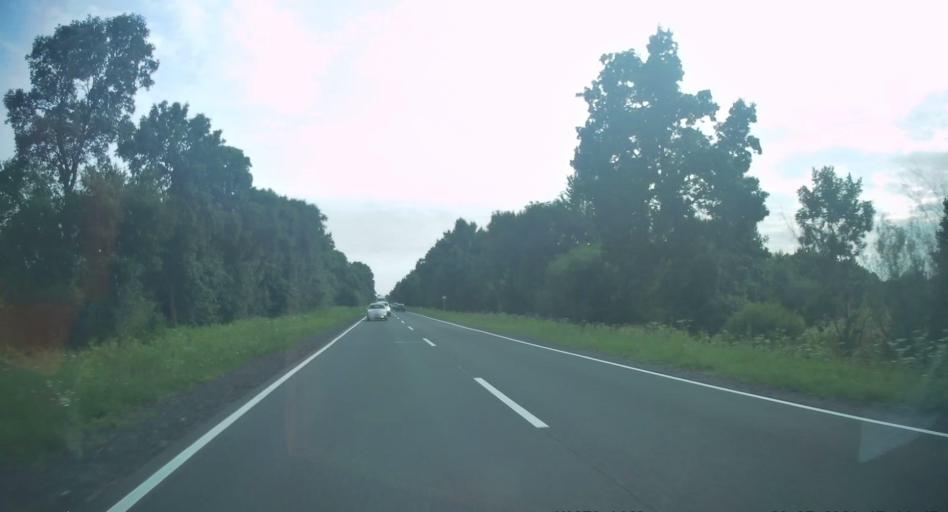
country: PL
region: Silesian Voivodeship
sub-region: Powiat czestochowski
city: Klomnice
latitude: 50.9405
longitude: 19.3890
